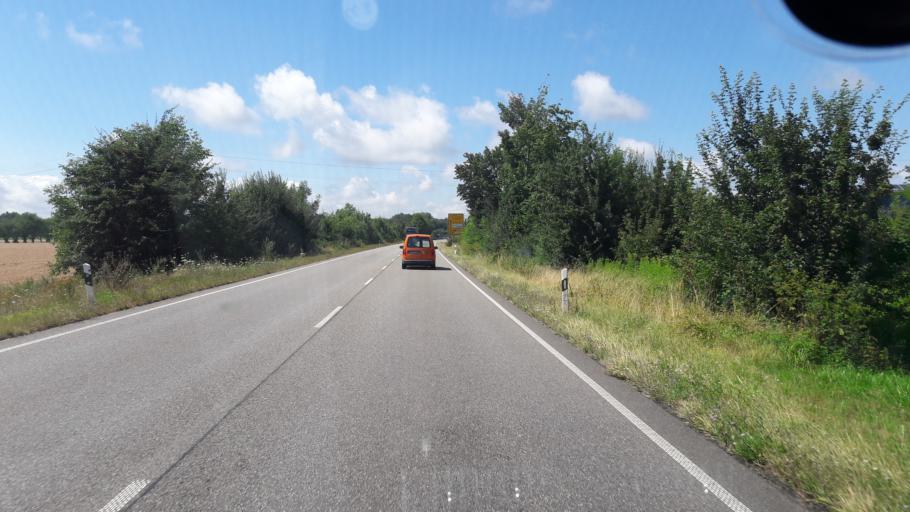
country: DE
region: Baden-Wuerttemberg
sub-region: Karlsruhe Region
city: Philippsburg
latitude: 49.1942
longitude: 8.4609
